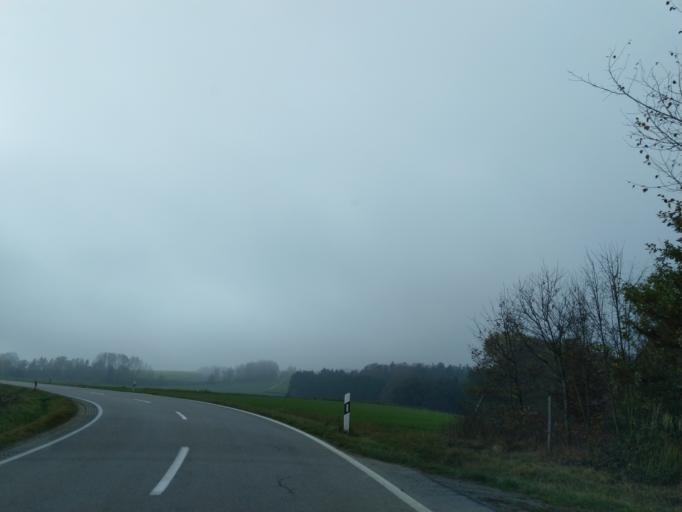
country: DE
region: Bavaria
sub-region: Lower Bavaria
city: Schollnach
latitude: 48.7779
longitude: 13.1702
